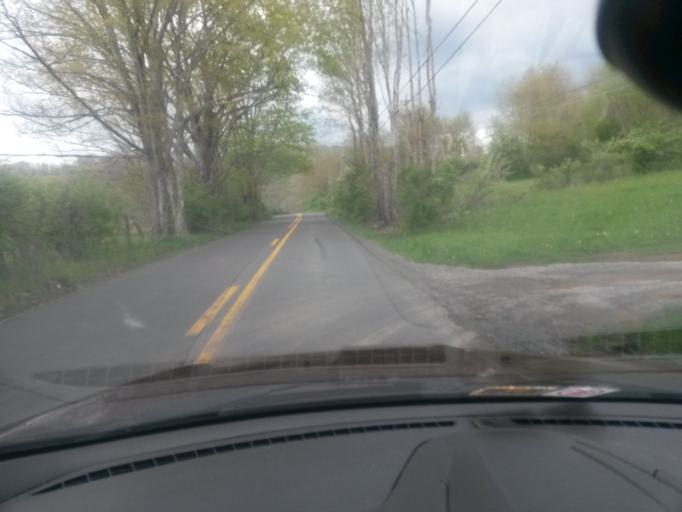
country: US
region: West Virginia
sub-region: Greenbrier County
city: Lewisburg
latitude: 37.9340
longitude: -80.4040
